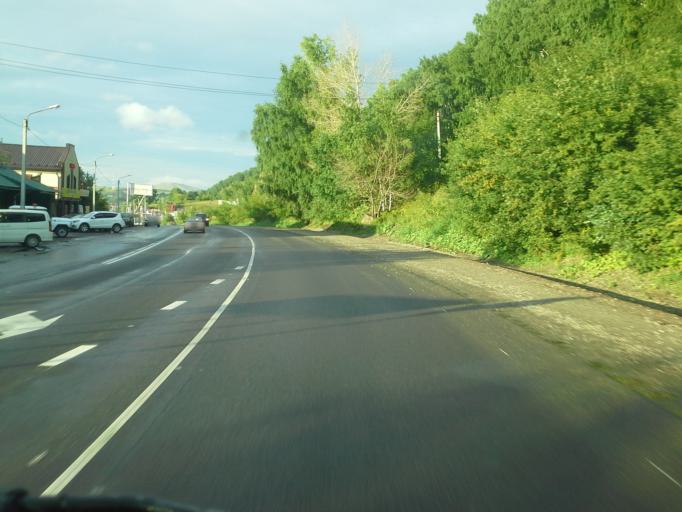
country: RU
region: Khabarovsk Krai
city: Mayma
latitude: 52.0051
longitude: 85.9073
